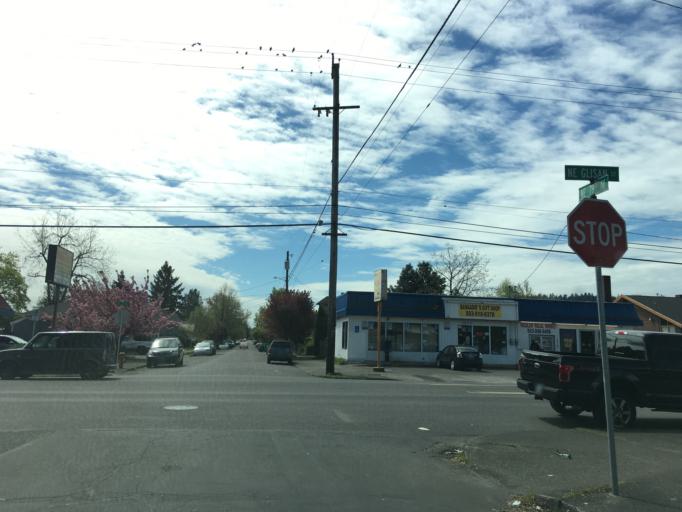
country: US
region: Oregon
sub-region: Multnomah County
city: Lents
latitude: 45.5267
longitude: -122.5824
